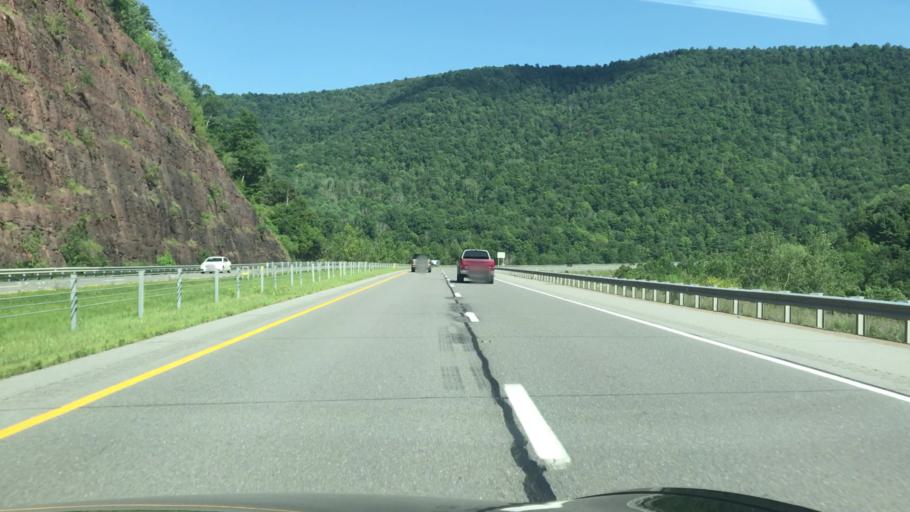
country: US
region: Pennsylvania
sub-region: Lycoming County
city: Garden View
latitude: 41.3451
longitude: -77.0914
